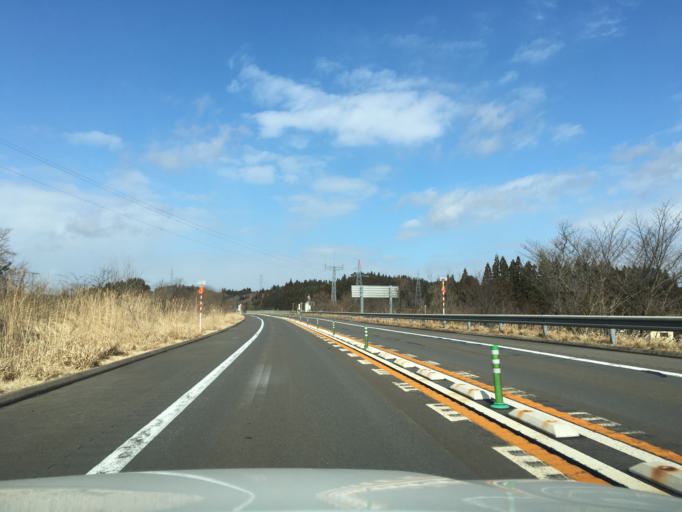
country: JP
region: Akita
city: Akita
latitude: 39.7381
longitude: 140.1725
